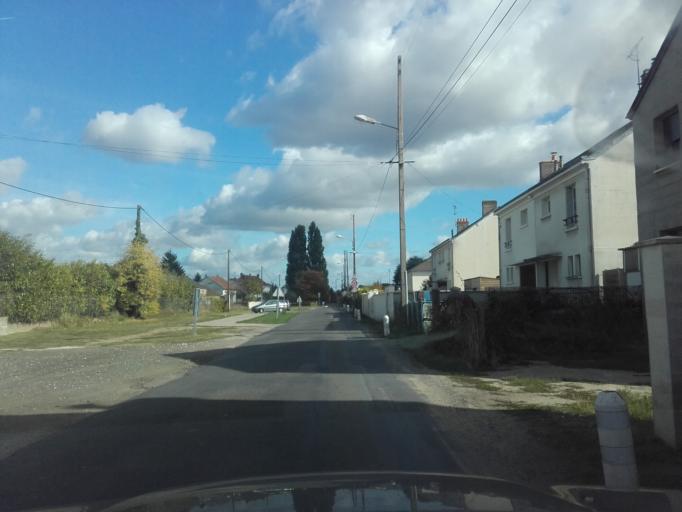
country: FR
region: Centre
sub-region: Departement d'Indre-et-Loire
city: Saint-Pierre-des-Corps
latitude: 47.3912
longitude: 0.7459
